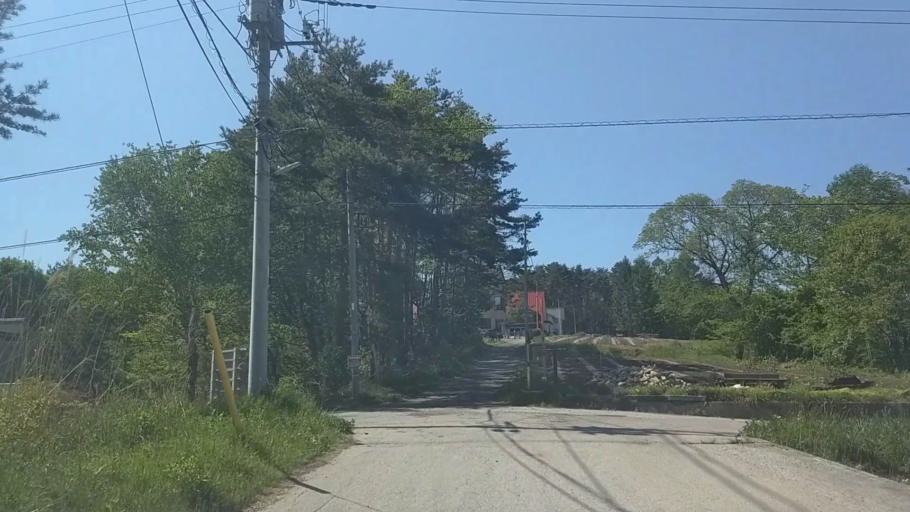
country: JP
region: Yamanashi
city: Nirasaki
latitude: 35.9066
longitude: 138.4402
